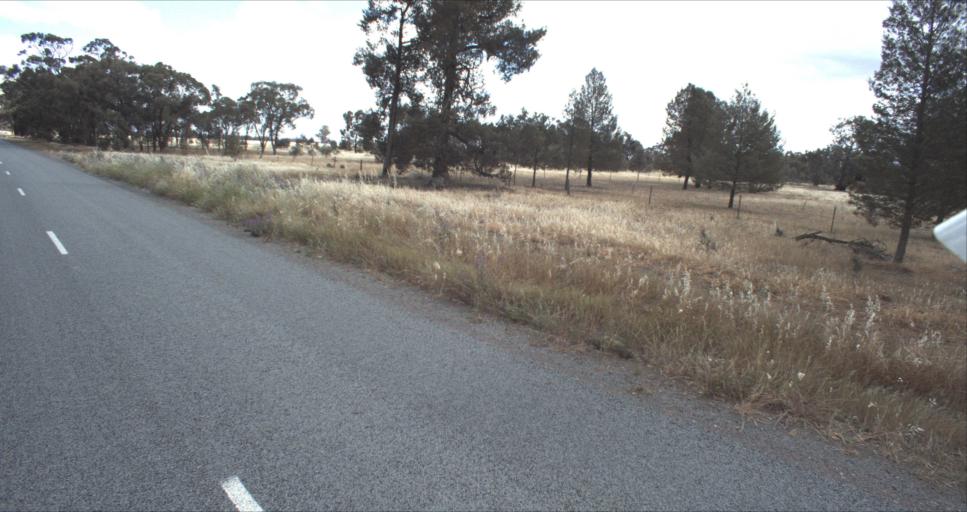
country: AU
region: New South Wales
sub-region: Leeton
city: Leeton
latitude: -34.6657
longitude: 146.3484
